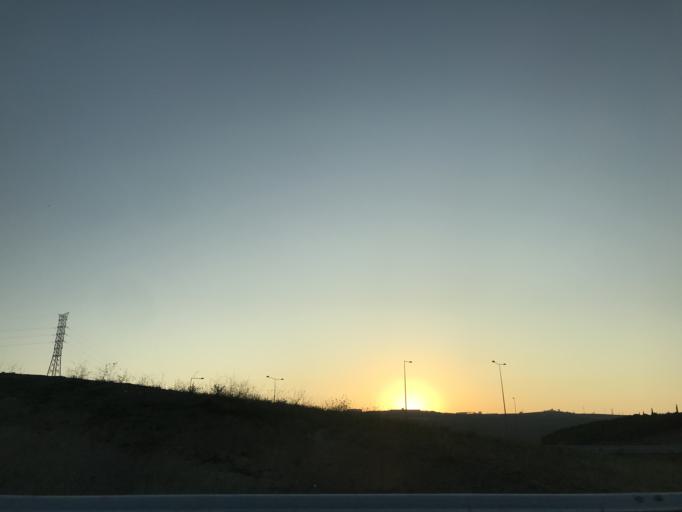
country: TR
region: Kocaeli
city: Tavsanli
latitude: 40.8085
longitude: 29.5191
